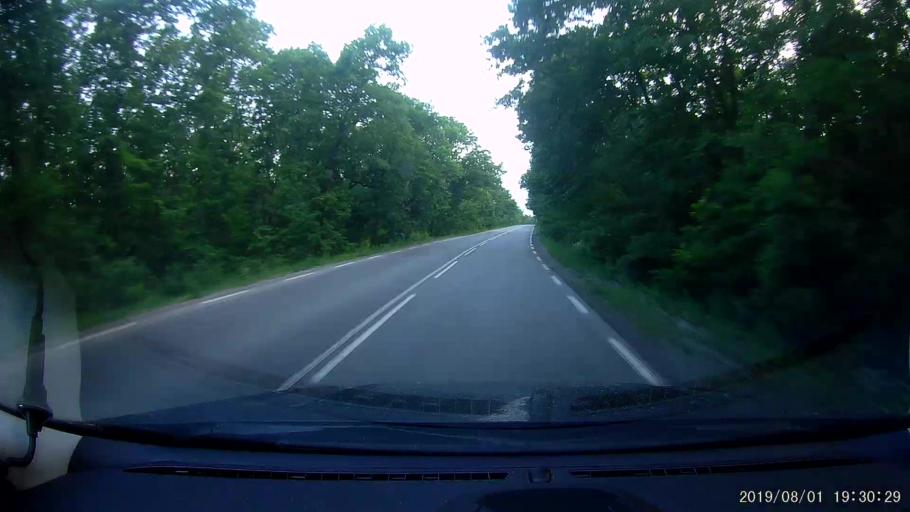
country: BG
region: Burgas
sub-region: Obshtina Sungurlare
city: Sungurlare
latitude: 42.8133
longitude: 26.8924
